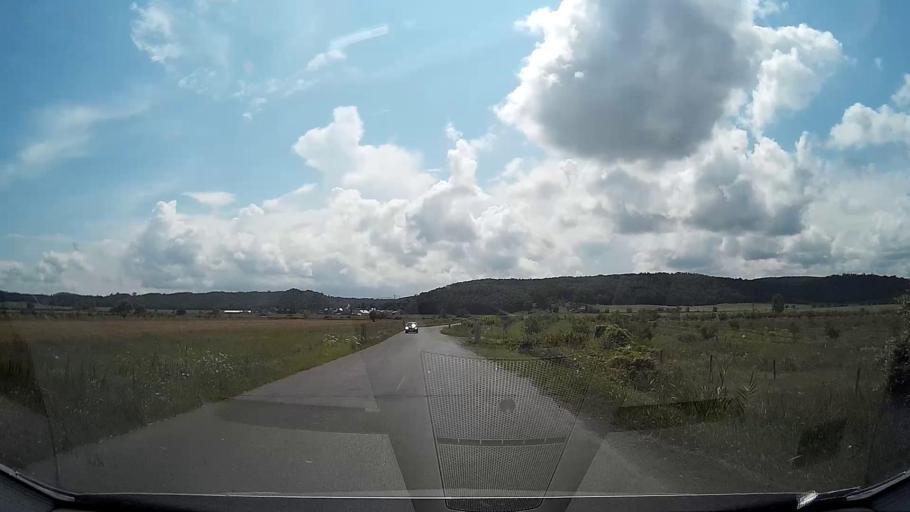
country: SK
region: Banskobystricky
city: Fil'akovo
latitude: 48.2961
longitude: 19.7911
